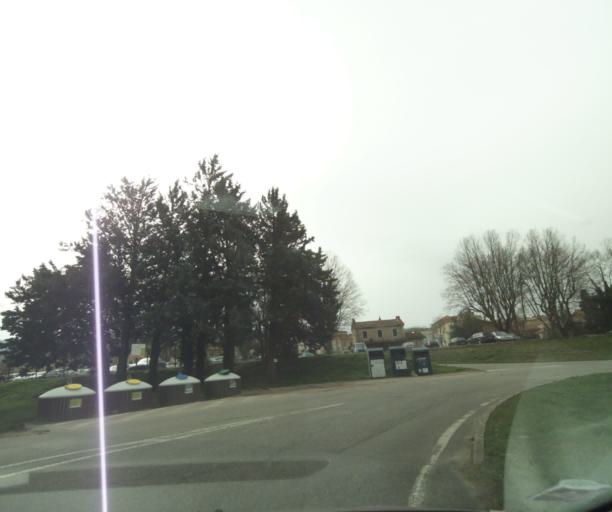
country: FR
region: Provence-Alpes-Cote d'Azur
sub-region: Departement des Bouches-du-Rhone
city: Trets
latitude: 43.4498
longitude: 5.6876
